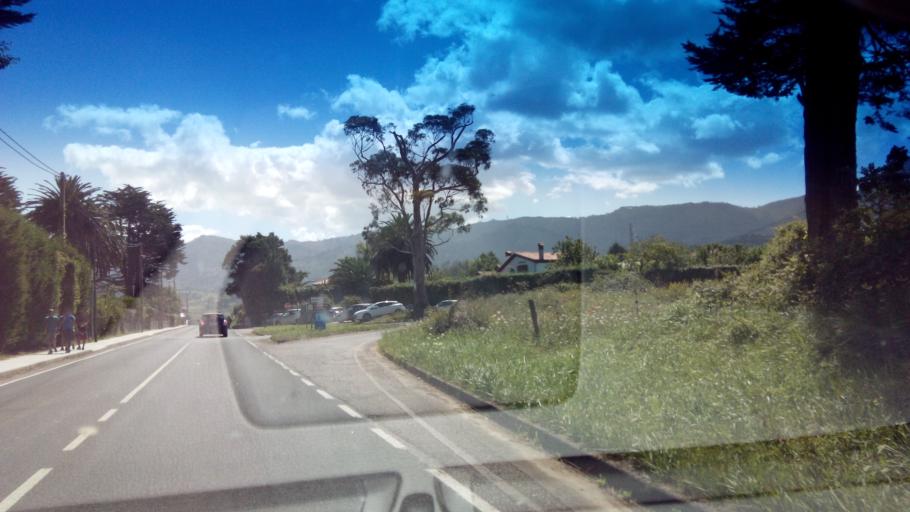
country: ES
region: Asturias
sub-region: Province of Asturias
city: Colunga
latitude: 43.4764
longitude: -5.2233
